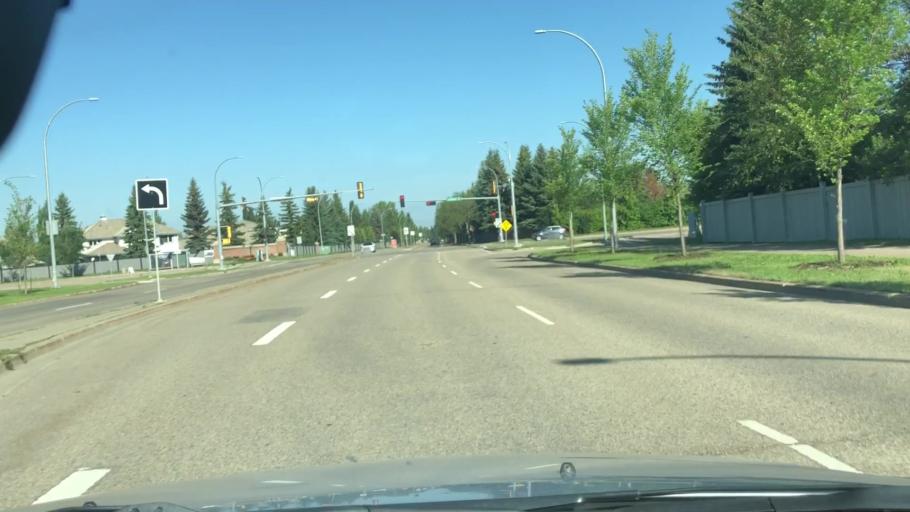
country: CA
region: Alberta
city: Edmonton
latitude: 53.4716
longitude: -113.5930
